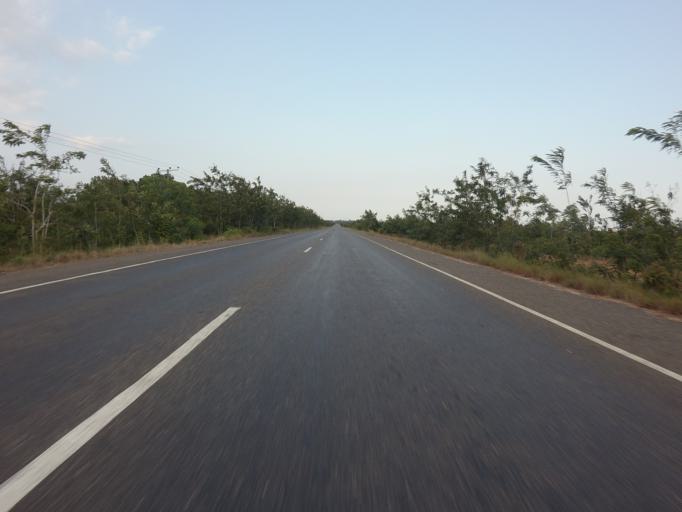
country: GH
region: Volta
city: Anloga
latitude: 6.0787
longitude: 0.5875
